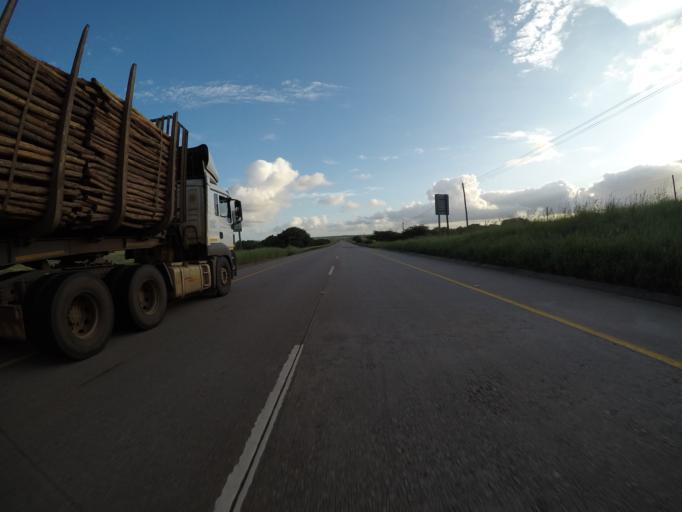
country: ZA
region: KwaZulu-Natal
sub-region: uMkhanyakude District Municipality
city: Mtubatuba
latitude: -28.4895
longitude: 32.1411
